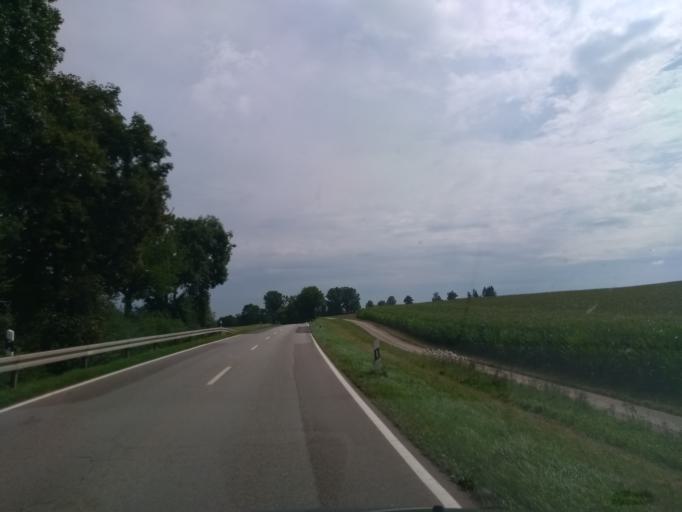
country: DE
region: Bavaria
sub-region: Upper Bavaria
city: Markt Indersdorf
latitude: 48.3757
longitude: 11.3627
